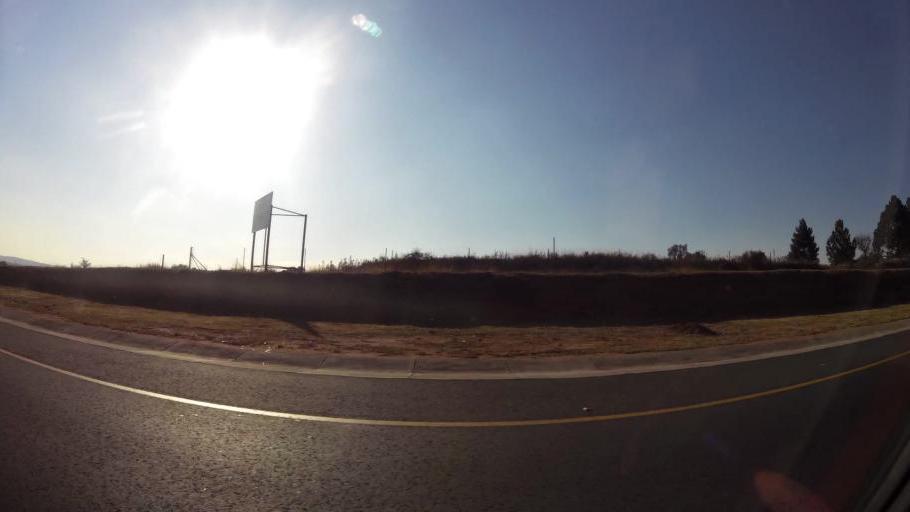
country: ZA
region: Gauteng
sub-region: West Rand District Municipality
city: Muldersdriseloop
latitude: -26.0127
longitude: 27.8792
